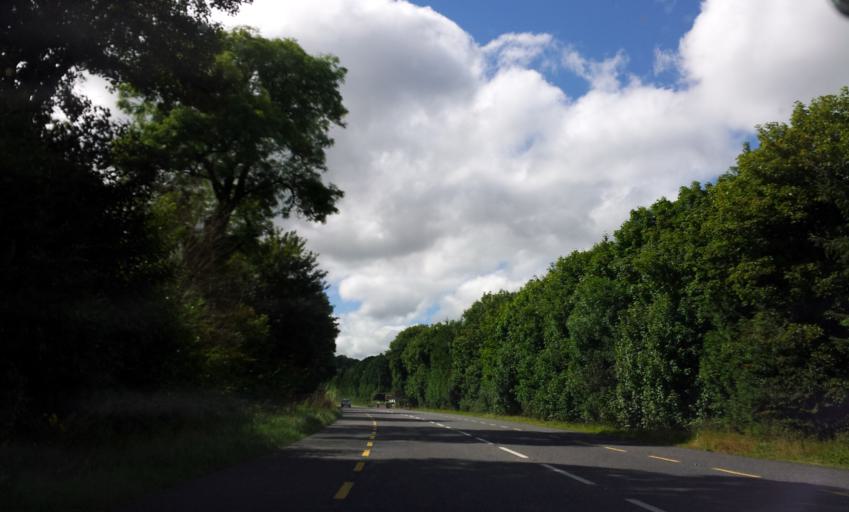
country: IE
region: Munster
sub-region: County Cork
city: Killumney
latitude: 51.8820
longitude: -8.6653
